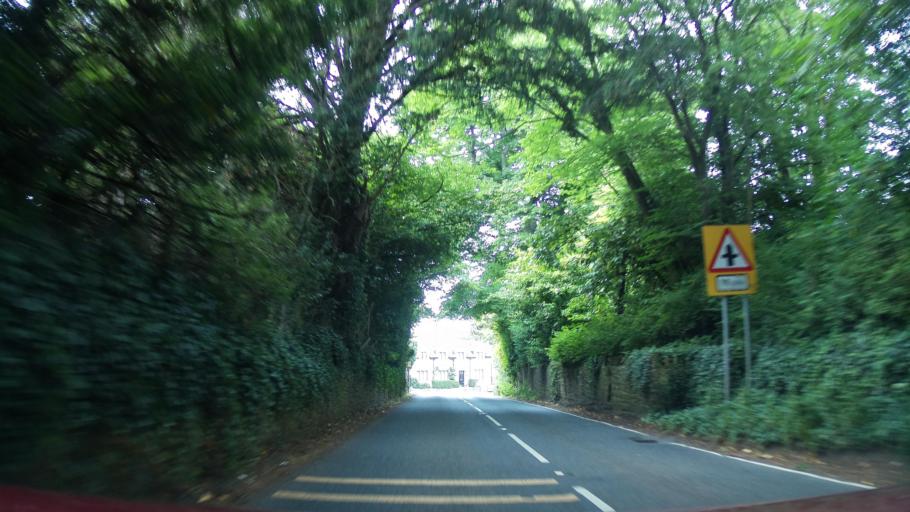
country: GB
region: England
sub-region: Somerset
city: Crewkerne
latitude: 50.8932
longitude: -2.7522
